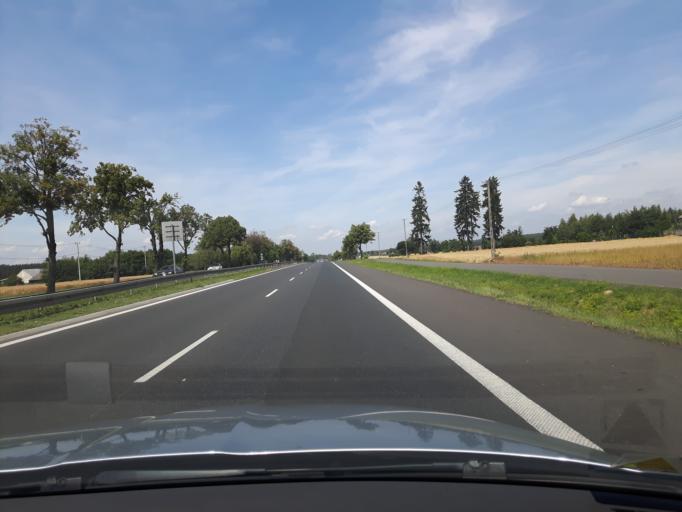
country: PL
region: Masovian Voivodeship
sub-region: Powiat plonski
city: Zaluski
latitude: 52.4884
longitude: 20.5478
